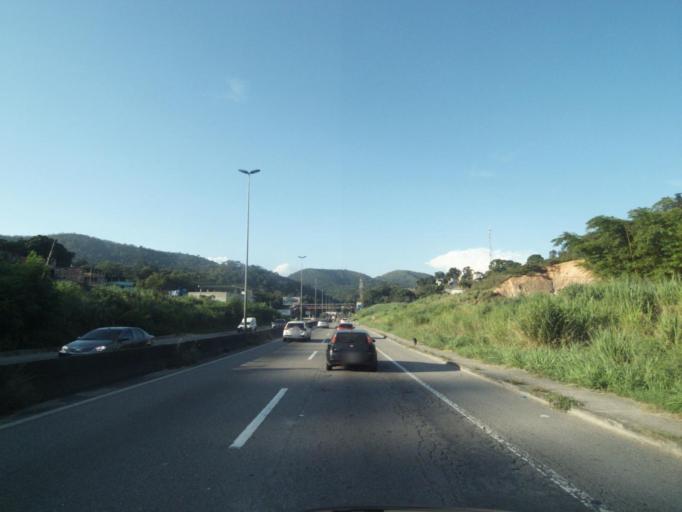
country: BR
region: Rio de Janeiro
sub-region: Niteroi
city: Niteroi
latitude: -22.8789
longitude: -43.0561
